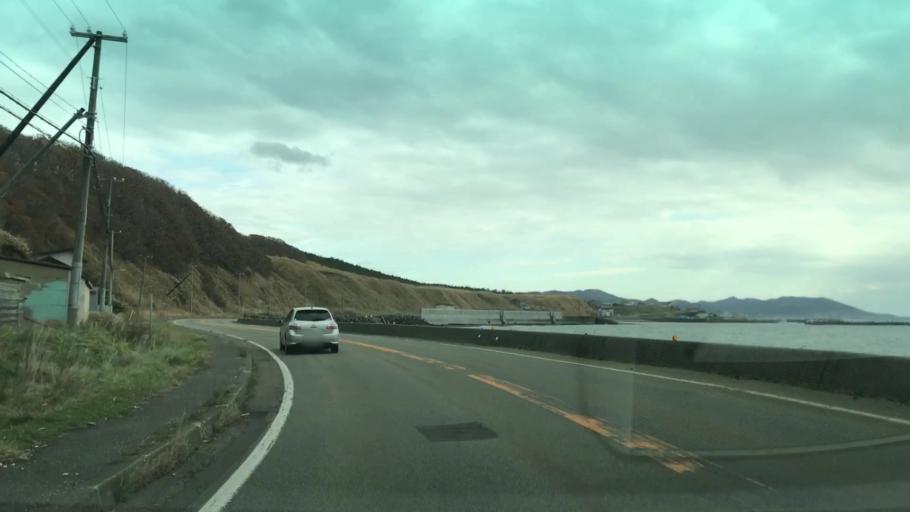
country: JP
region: Hokkaido
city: Shizunai-furukawacho
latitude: 42.0510
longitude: 143.0918
